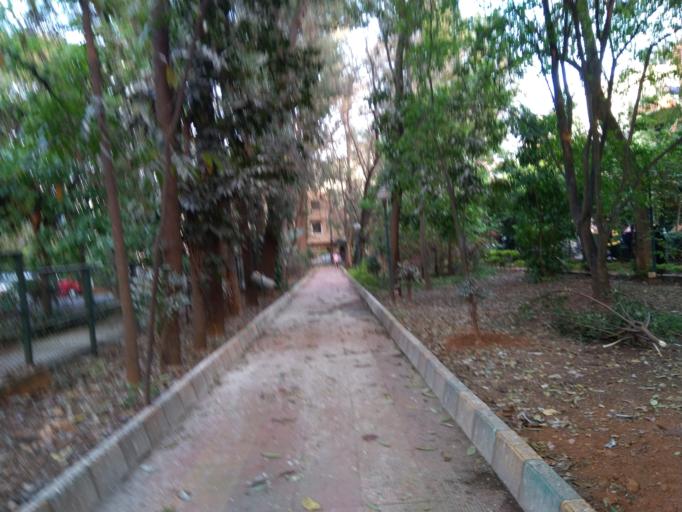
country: IN
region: Karnataka
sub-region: Bangalore Urban
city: Bangalore
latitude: 12.9104
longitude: 77.6119
